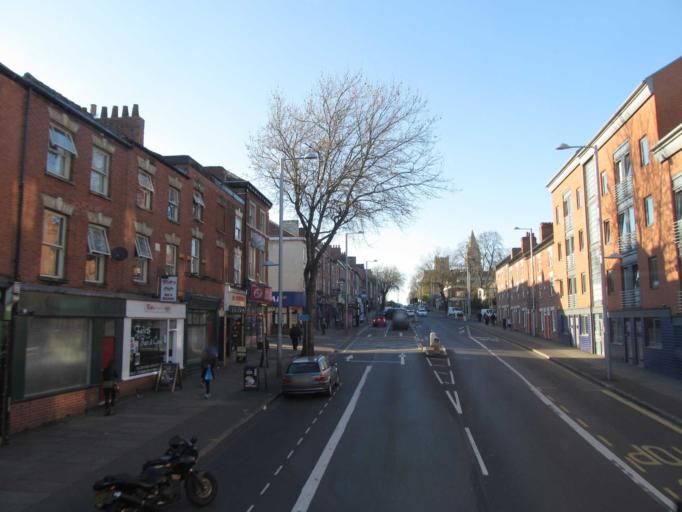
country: GB
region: England
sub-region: Nottingham
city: Nottingham
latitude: 52.9622
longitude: -1.1512
